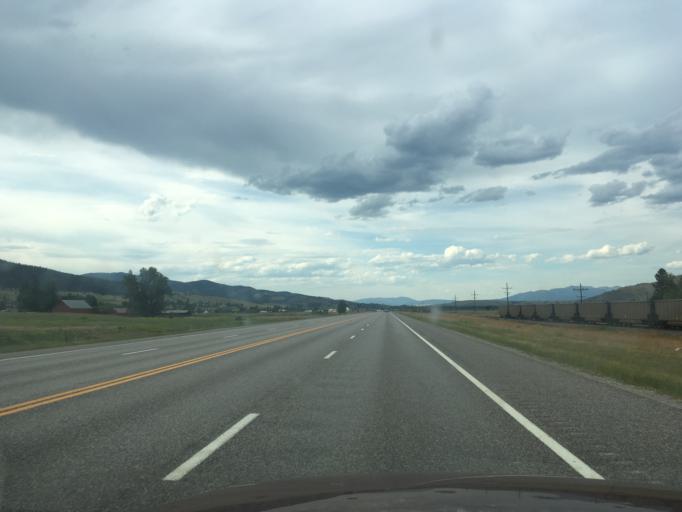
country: US
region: Montana
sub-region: Missoula County
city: Lolo
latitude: 46.7014
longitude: -114.0743
